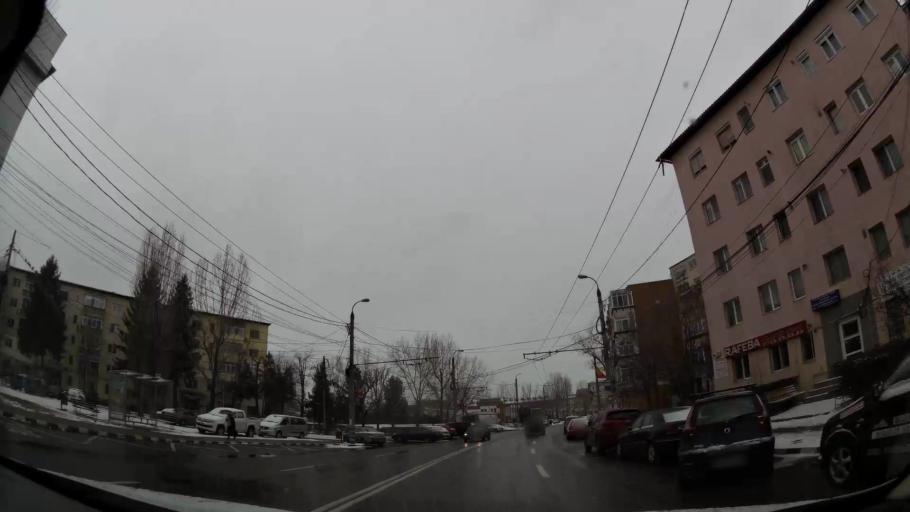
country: RO
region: Dambovita
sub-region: Municipiul Targoviste
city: Targoviste
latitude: 44.9198
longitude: 25.4682
